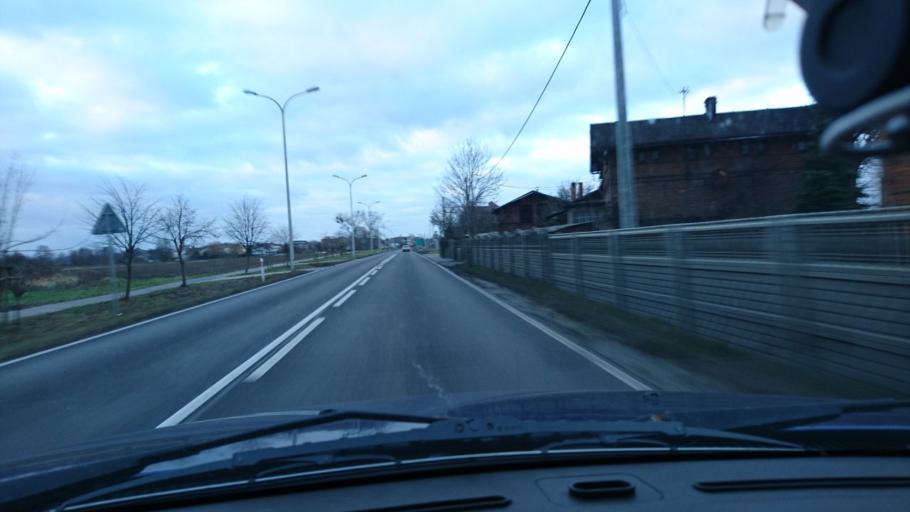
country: PL
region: Greater Poland Voivodeship
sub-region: Powiat kepinski
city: Kepno
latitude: 51.3020
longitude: 17.9941
